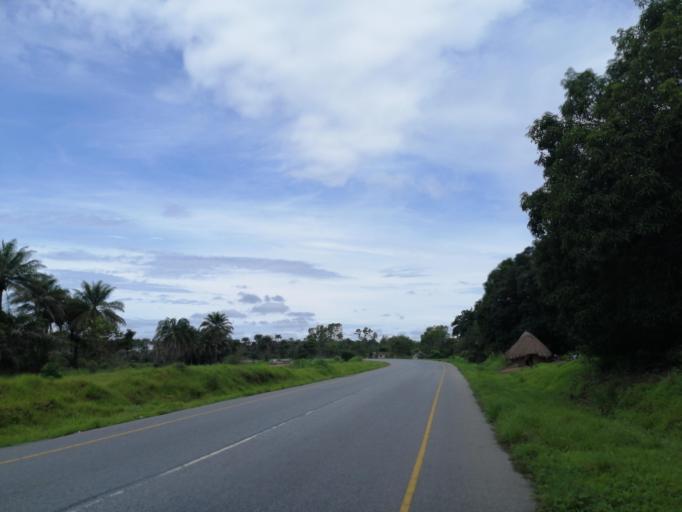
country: SL
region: Northern Province
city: Port Loko
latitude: 8.7553
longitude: -12.9152
